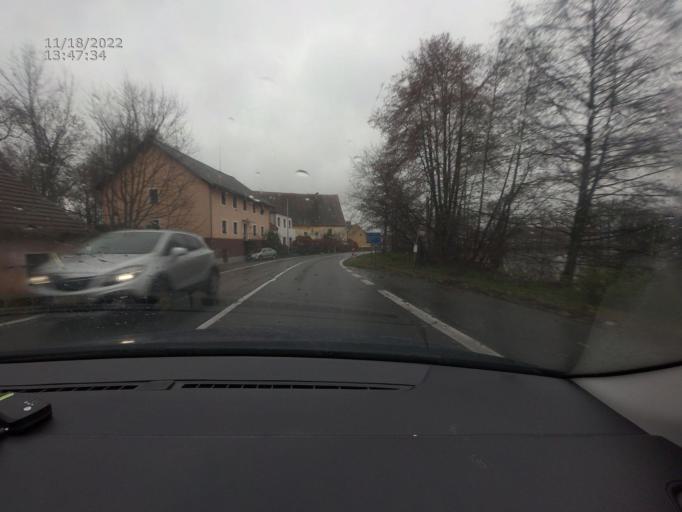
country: CZ
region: Jihocesky
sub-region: Okres Strakonice
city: Blatna
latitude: 49.4221
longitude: 13.8770
